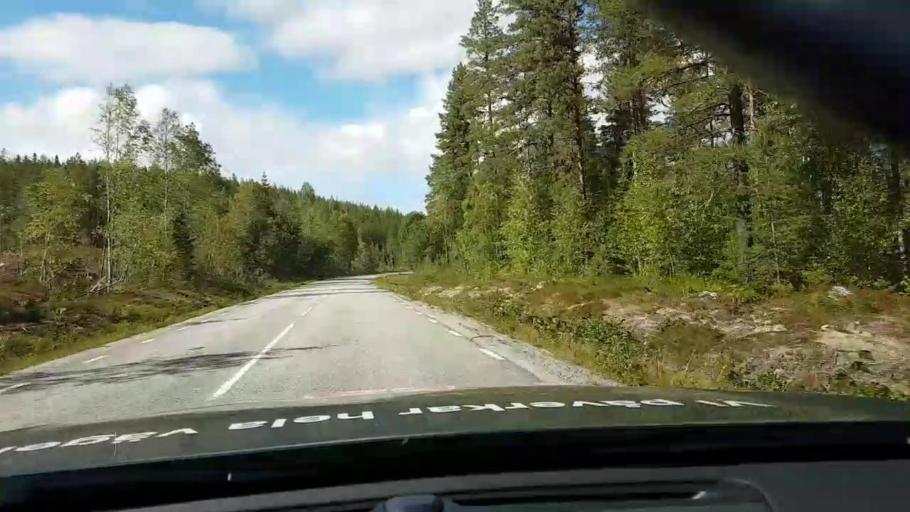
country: SE
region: Vaesternorrland
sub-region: OErnskoeldsviks Kommun
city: Bredbyn
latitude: 63.6624
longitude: 17.8425
